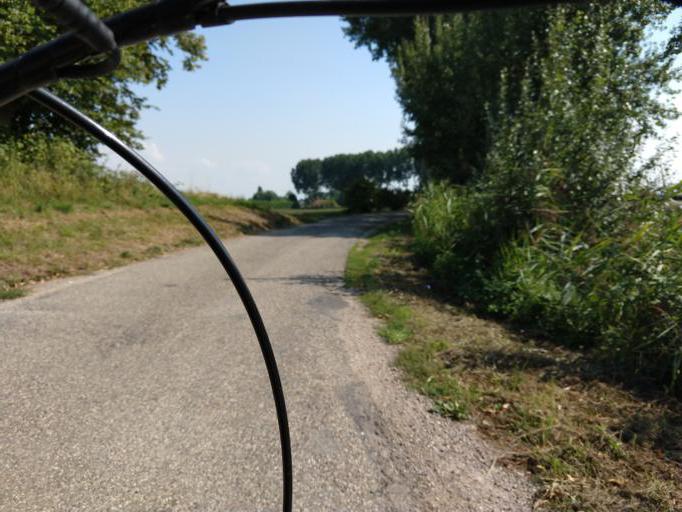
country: NL
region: Zeeland
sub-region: Gemeente Goes
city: Goes
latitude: 51.4383
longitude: 3.8790
